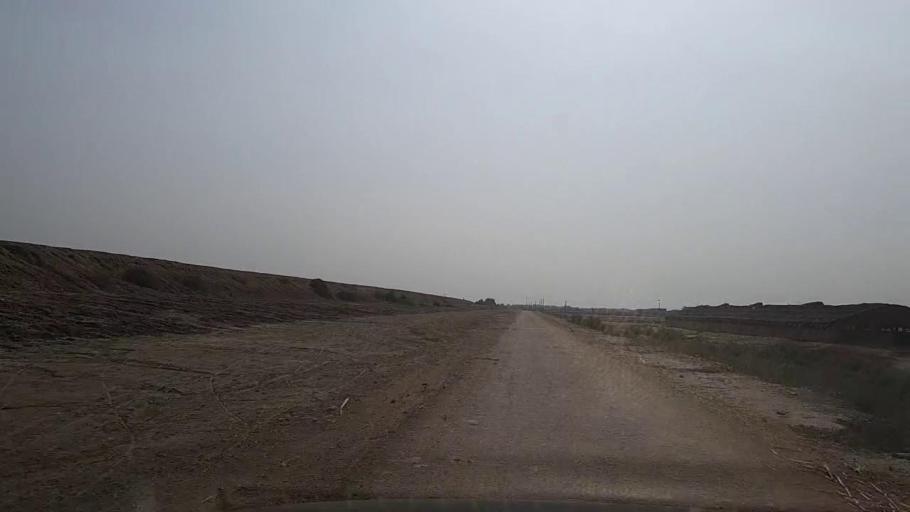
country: PK
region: Sindh
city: Thatta
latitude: 24.5667
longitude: 67.9132
